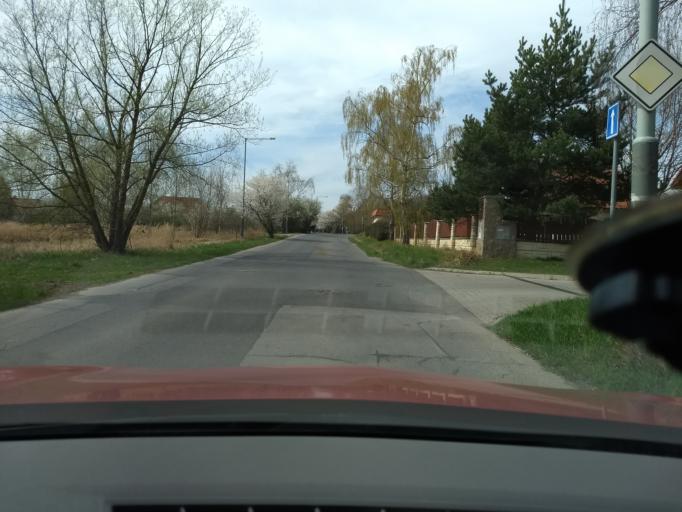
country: CZ
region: Central Bohemia
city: Hostivice
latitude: 50.0668
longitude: 14.2618
